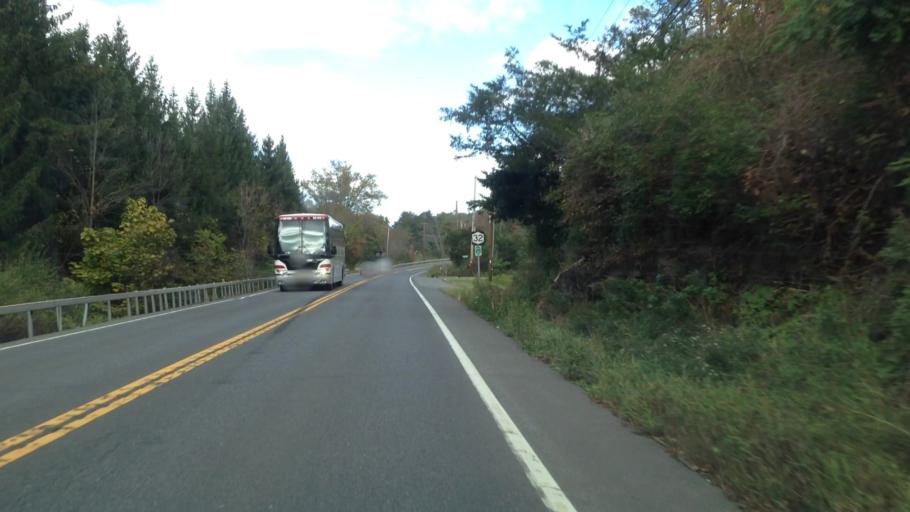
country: US
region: New York
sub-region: Ulster County
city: Tillson
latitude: 41.7992
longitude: -74.0659
